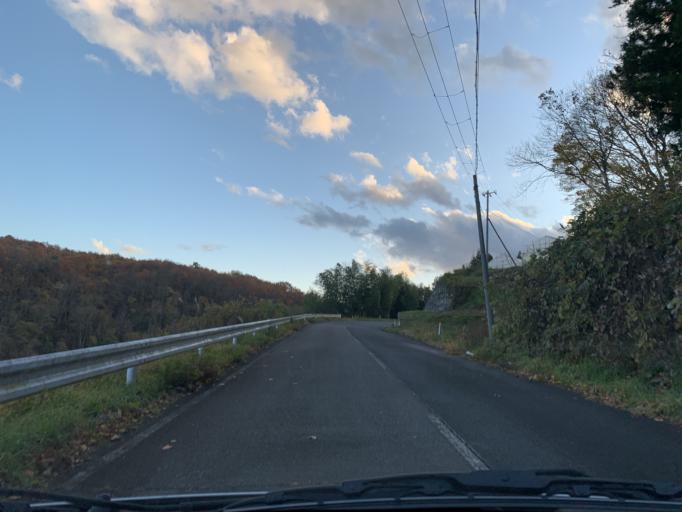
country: JP
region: Iwate
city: Mizusawa
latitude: 39.0273
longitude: 141.0362
